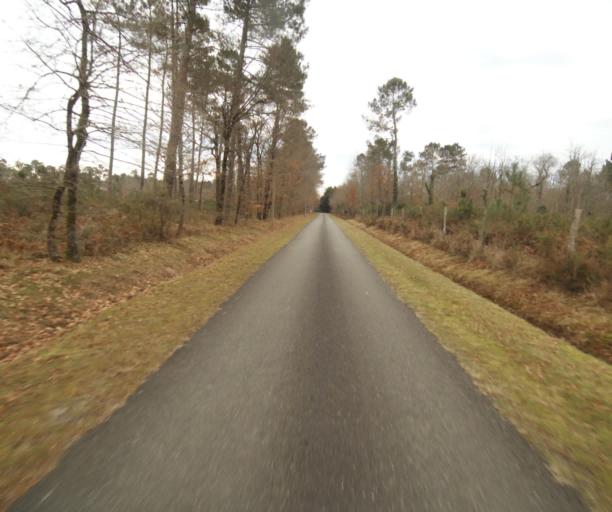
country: FR
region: Midi-Pyrenees
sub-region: Departement du Gers
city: Cazaubon
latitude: 44.0203
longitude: -0.0705
